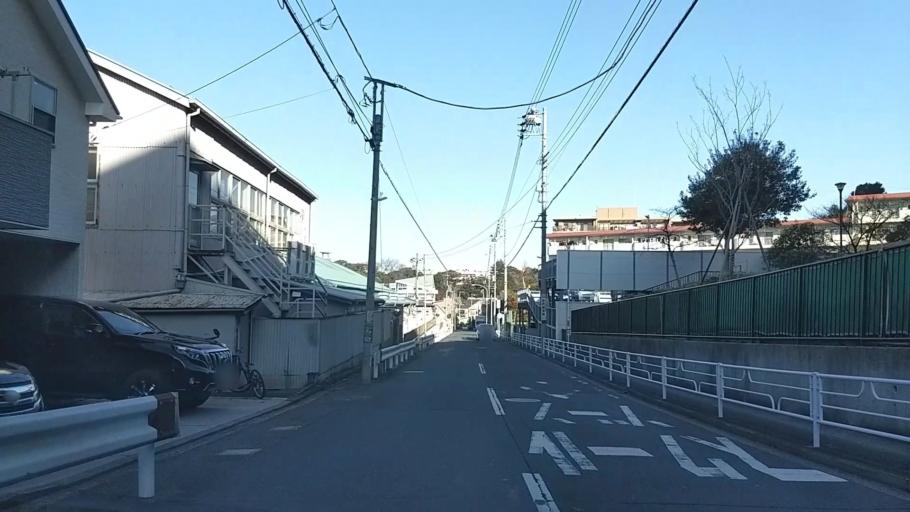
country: JP
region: Kanagawa
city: Yokohama
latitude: 35.4222
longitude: 139.6121
